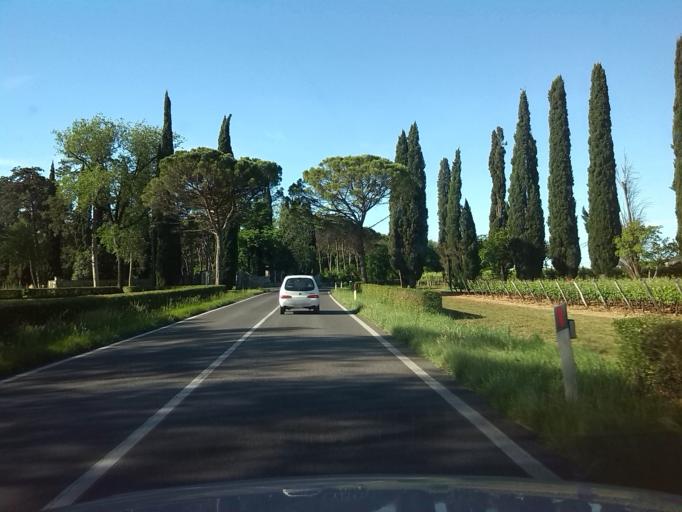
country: IT
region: Friuli Venezia Giulia
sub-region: Provincia di Gorizia
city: Cormons
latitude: 45.9392
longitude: 13.4585
